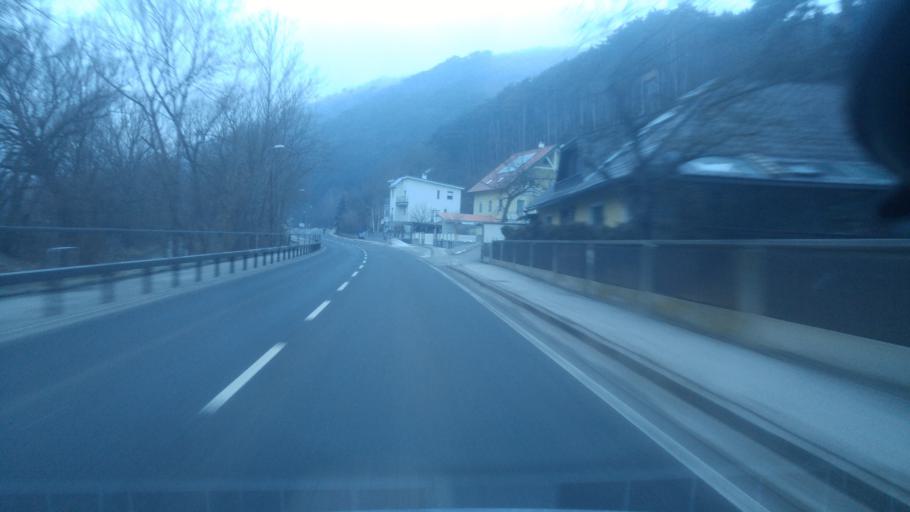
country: AT
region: Lower Austria
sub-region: Politischer Bezirk Baden
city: Weissenbach an der Triesting
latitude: 47.9822
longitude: 16.0634
